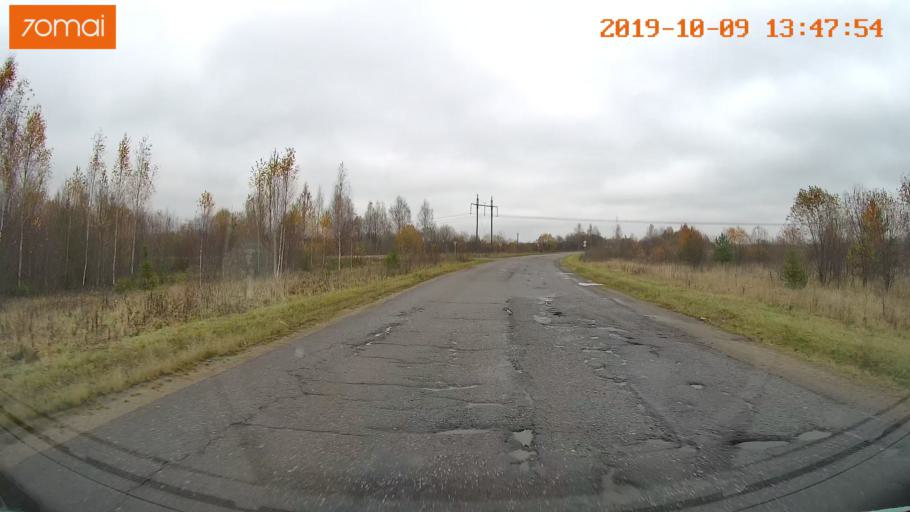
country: RU
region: Kostroma
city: Buy
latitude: 58.3964
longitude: 41.2275
